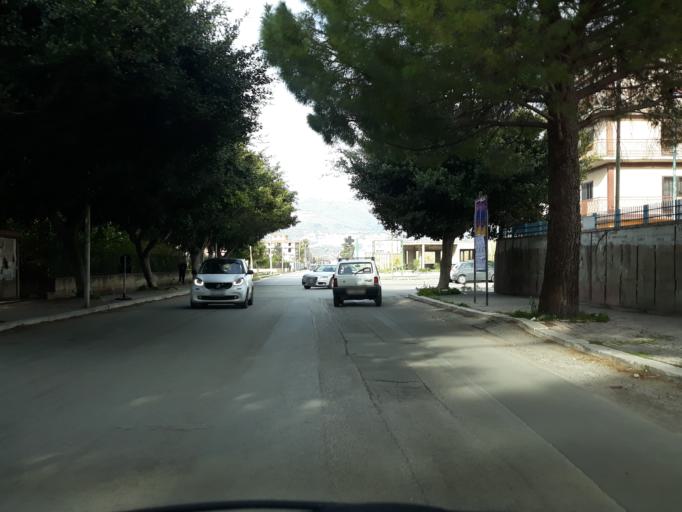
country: IT
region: Sicily
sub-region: Palermo
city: Partinico
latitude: 38.0519
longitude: 13.1255
